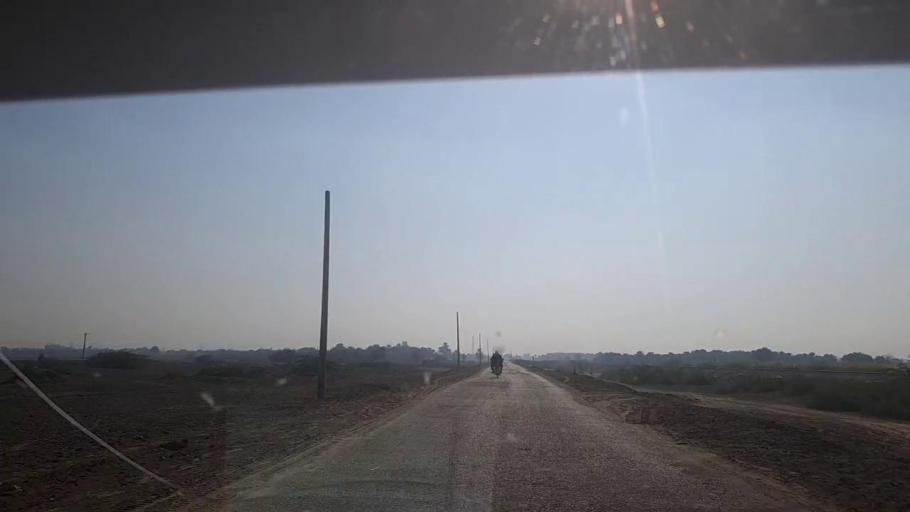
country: PK
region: Sindh
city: Gambat
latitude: 27.3552
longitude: 68.5524
